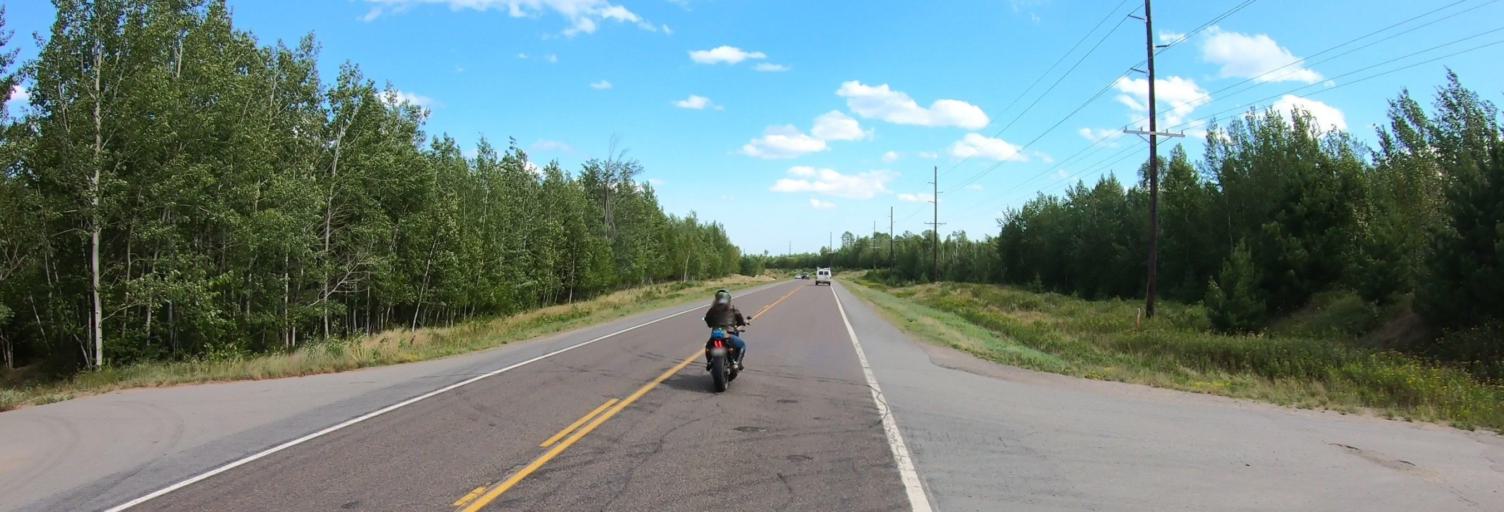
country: US
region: Minnesota
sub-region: Saint Louis County
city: Virginia
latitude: 47.8546
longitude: -92.4247
